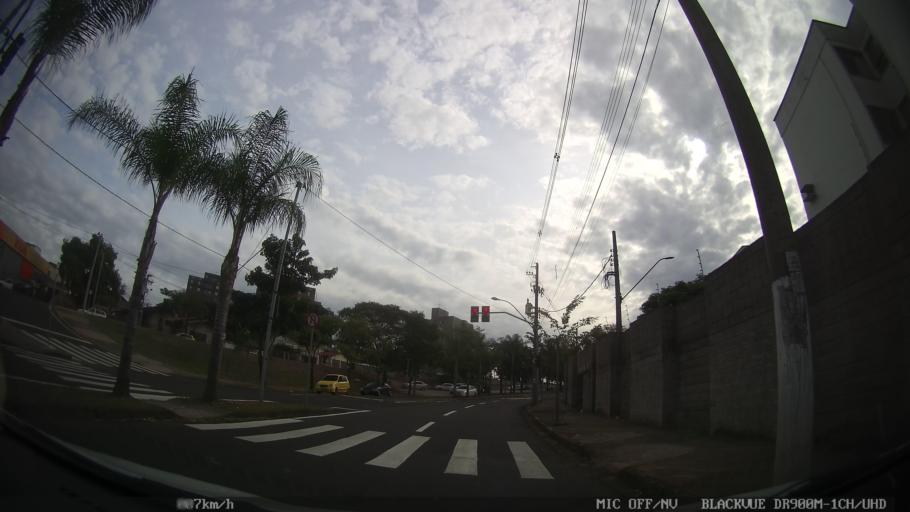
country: BR
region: Sao Paulo
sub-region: Piracicaba
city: Piracicaba
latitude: -22.7466
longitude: -47.6354
